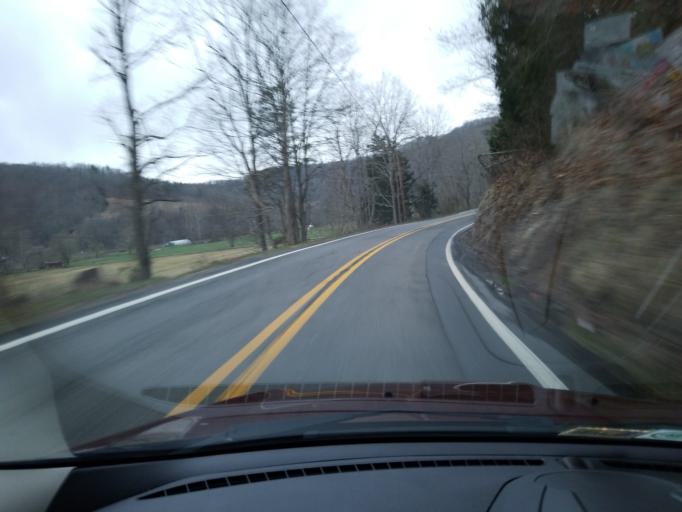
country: US
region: West Virginia
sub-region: Monroe County
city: Union
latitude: 37.5343
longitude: -80.5992
